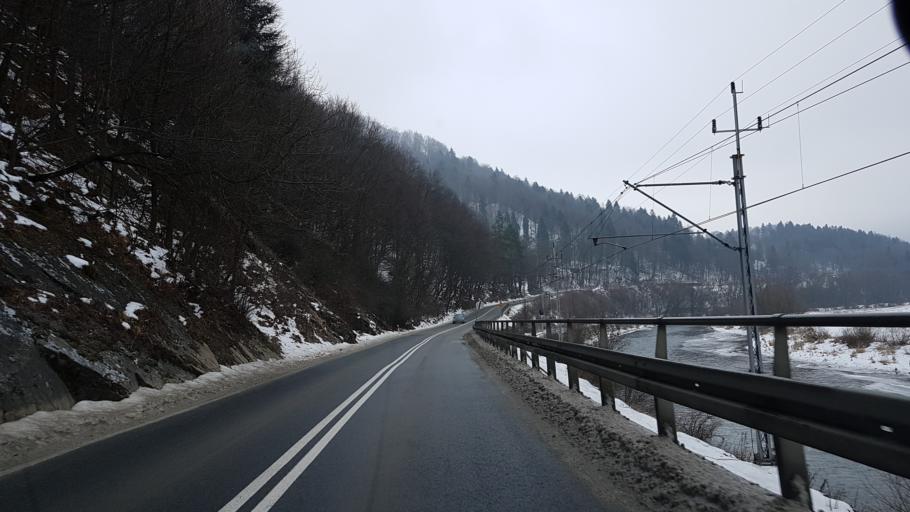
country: PL
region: Lesser Poland Voivodeship
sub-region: Powiat nowosadecki
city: Piwniczna-Zdroj
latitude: 49.4146
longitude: 20.7447
